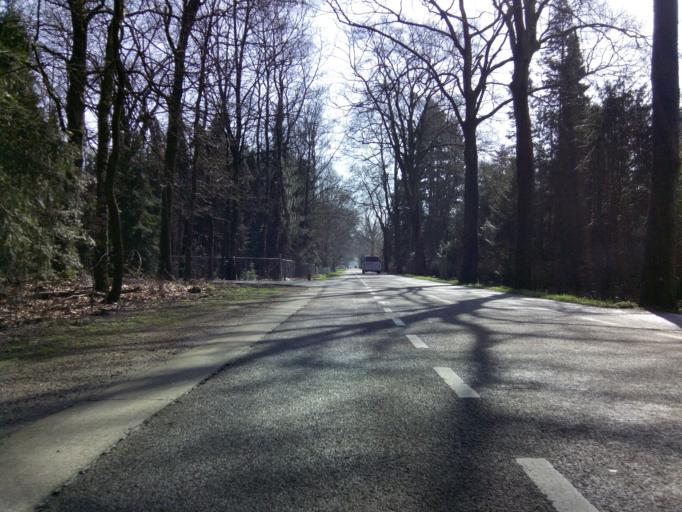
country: NL
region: Gelderland
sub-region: Gemeente Barneveld
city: Stroe
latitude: 52.1953
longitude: 5.6754
